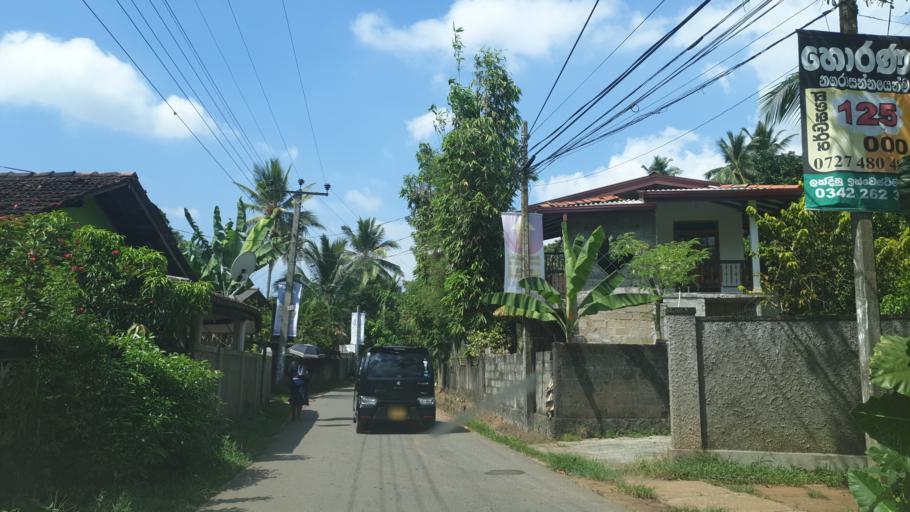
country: LK
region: Western
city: Horana South
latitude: 6.7090
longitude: 79.9829
